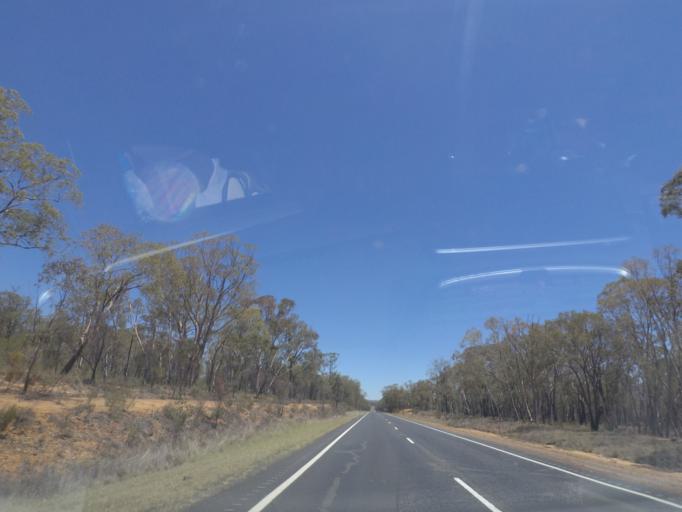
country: AU
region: New South Wales
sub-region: Warrumbungle Shire
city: Coonabarabran
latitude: -31.2129
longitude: 149.3291
